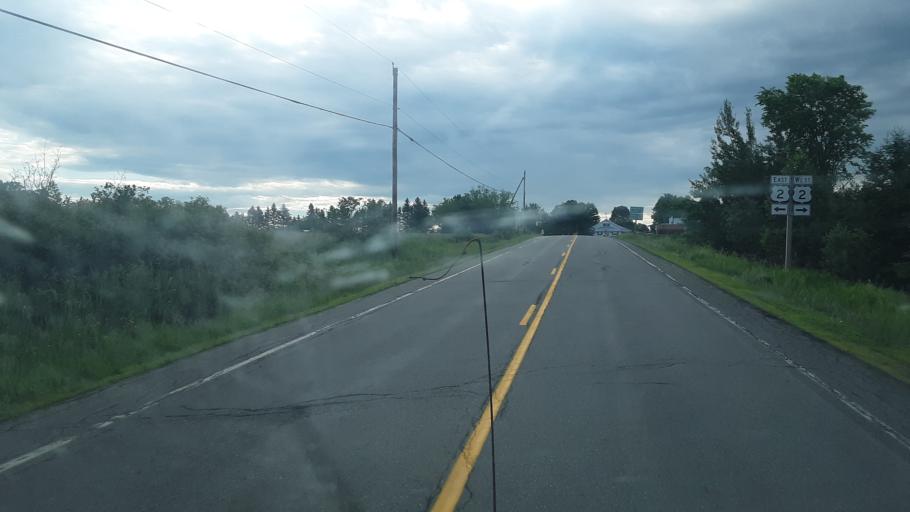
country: US
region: Maine
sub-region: Penobscot County
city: Patten
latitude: 45.8706
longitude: -68.3328
